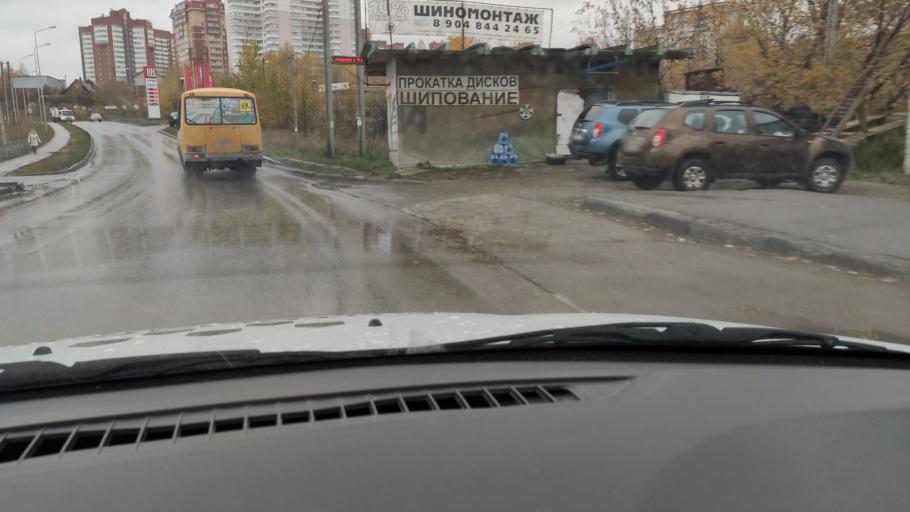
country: RU
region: Perm
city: Perm
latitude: 57.9812
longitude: 56.2797
